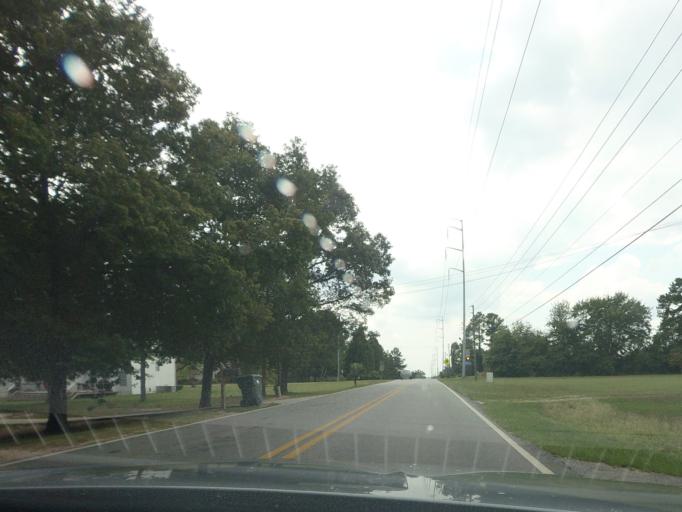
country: US
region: Georgia
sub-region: Bibb County
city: West Point
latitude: 32.8192
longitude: -83.7455
